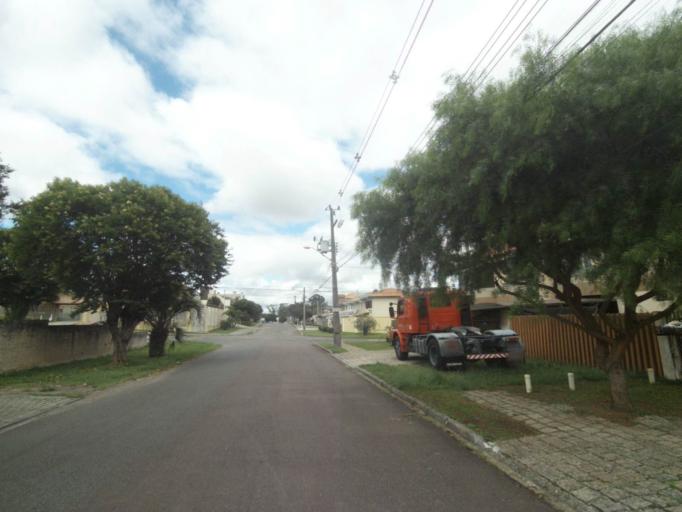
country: BR
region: Parana
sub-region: Curitiba
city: Curitiba
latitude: -25.4858
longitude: -49.2744
